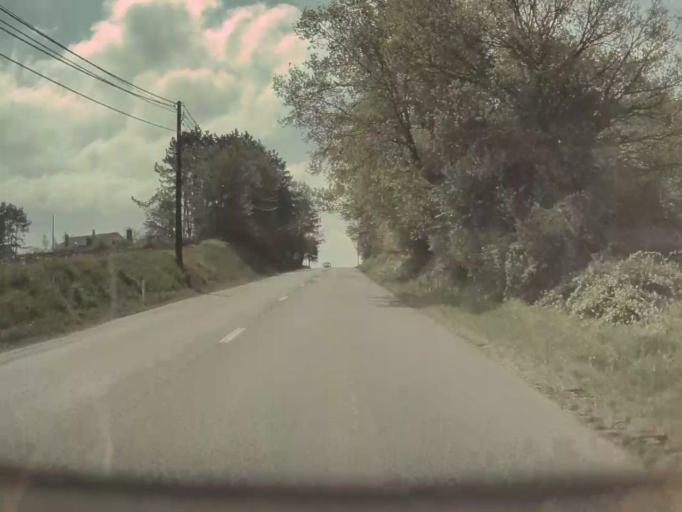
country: BE
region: Wallonia
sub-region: Province de Namur
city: Rochefort
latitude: 50.1390
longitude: 5.2241
